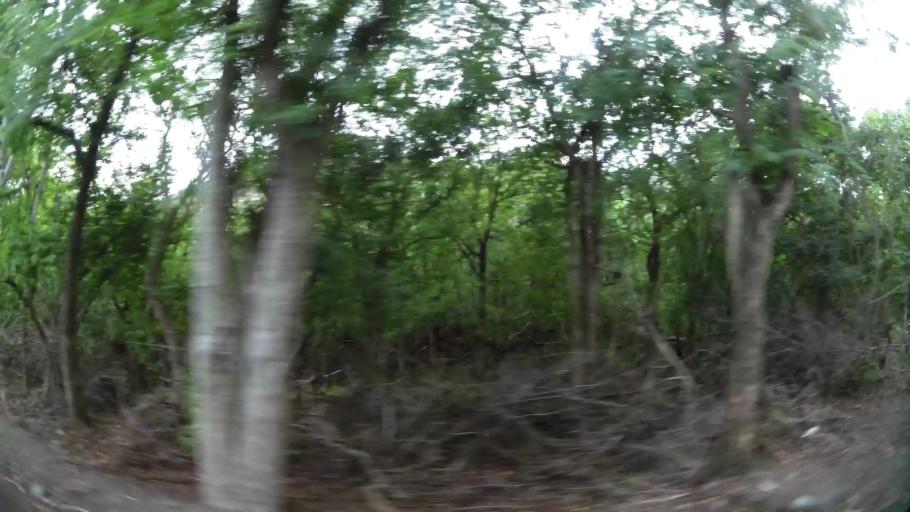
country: KN
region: Saint James Windwa
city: Newcastle
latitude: 17.2018
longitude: -62.5997
